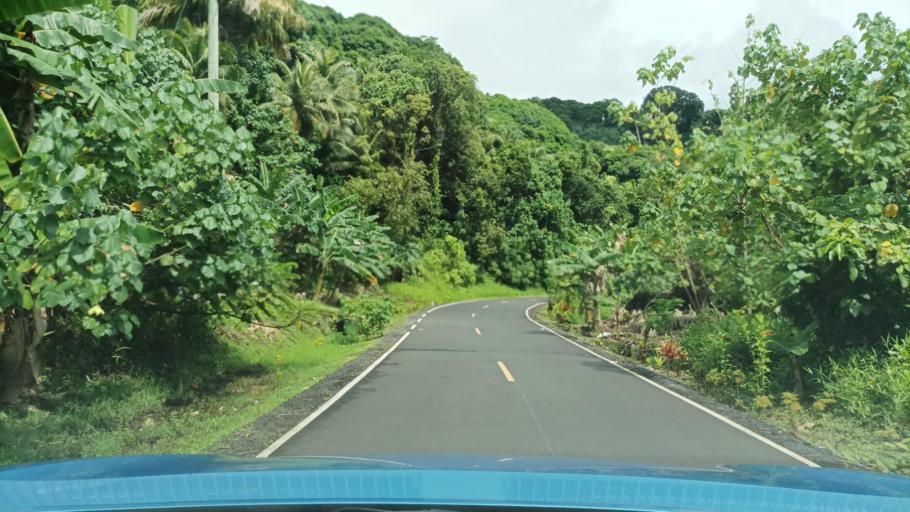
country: FM
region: Pohnpei
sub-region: Madolenihm Municipality
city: Madolenihm Municipality Government
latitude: 6.8698
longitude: 158.3289
